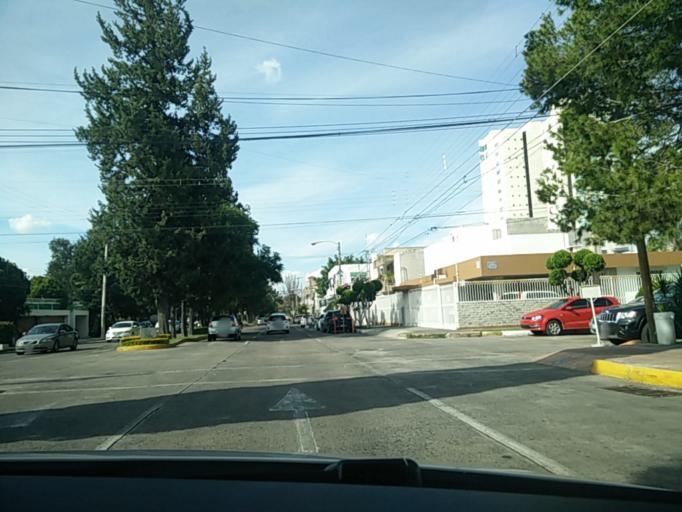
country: MX
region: Jalisco
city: Guadalajara
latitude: 20.6853
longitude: -103.3870
